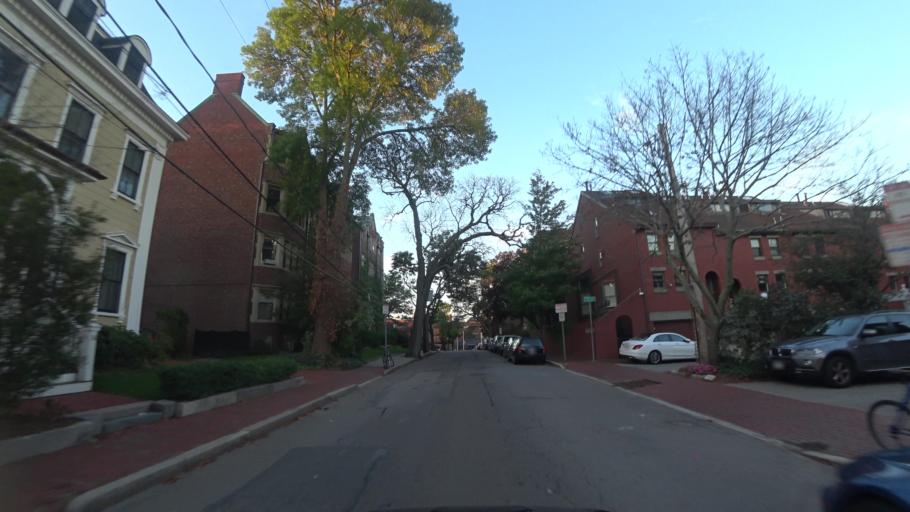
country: US
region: Massachusetts
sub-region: Middlesex County
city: Cambridge
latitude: 42.3707
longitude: -71.1097
